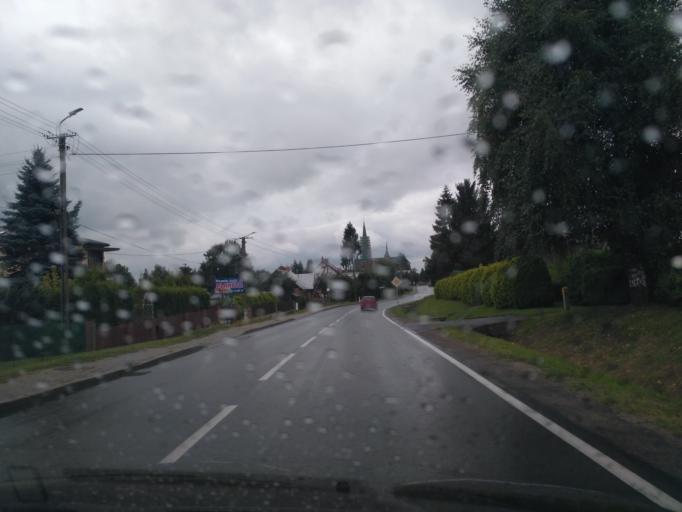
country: PL
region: Subcarpathian Voivodeship
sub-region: Powiat krosnienski
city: Korczyna
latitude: 49.7195
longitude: 21.8119
